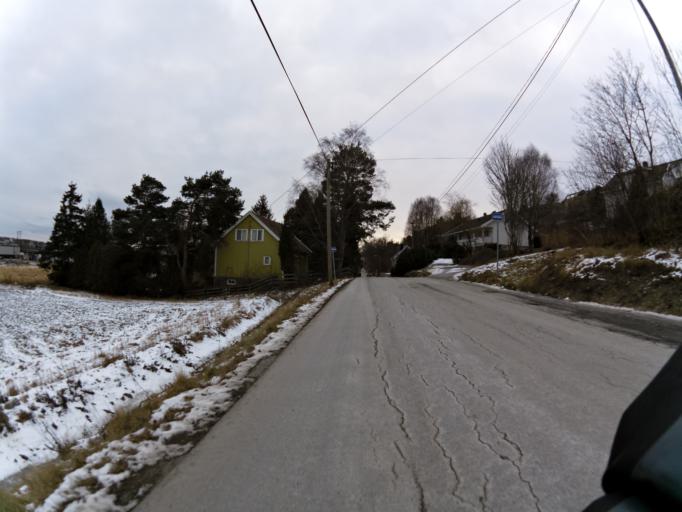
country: NO
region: Ostfold
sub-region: Fredrikstad
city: Fredrikstad
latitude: 59.2126
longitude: 10.8894
